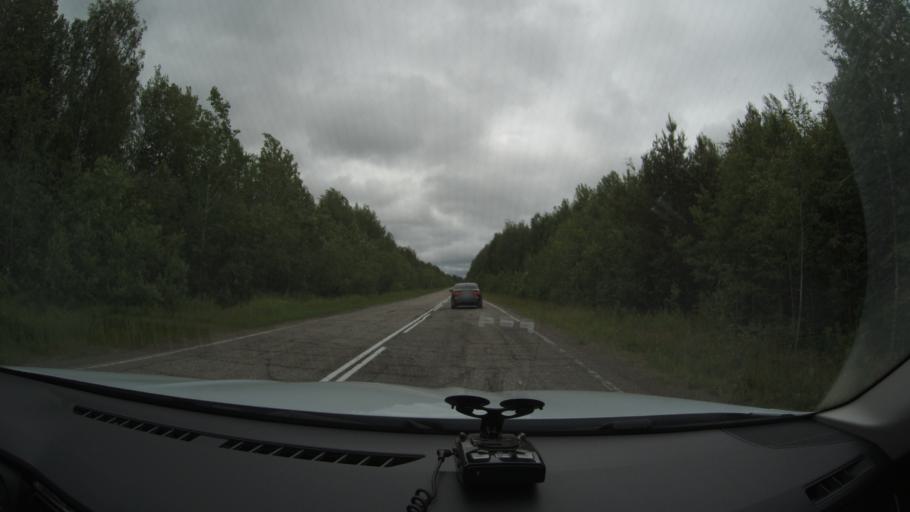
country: RU
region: Komi Republic
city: Nizhniy Odes
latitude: 63.6116
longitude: 54.5724
